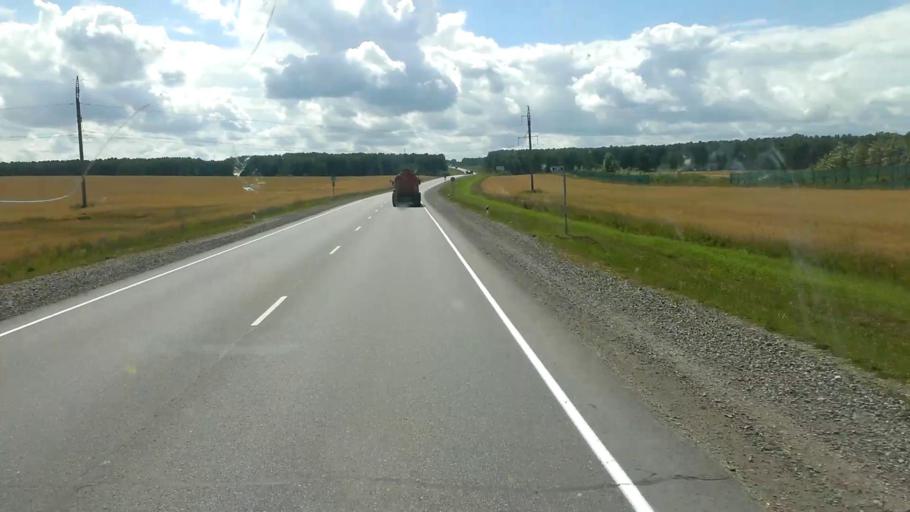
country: RU
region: Altai Krai
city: Troitskoye
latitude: 52.9902
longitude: 84.7426
